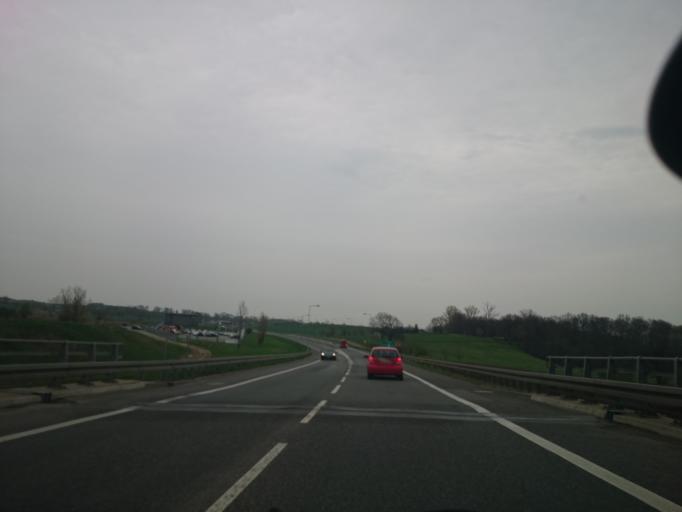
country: PL
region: Opole Voivodeship
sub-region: Powiat nyski
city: Otmuchow
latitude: 50.4585
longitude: 17.1928
